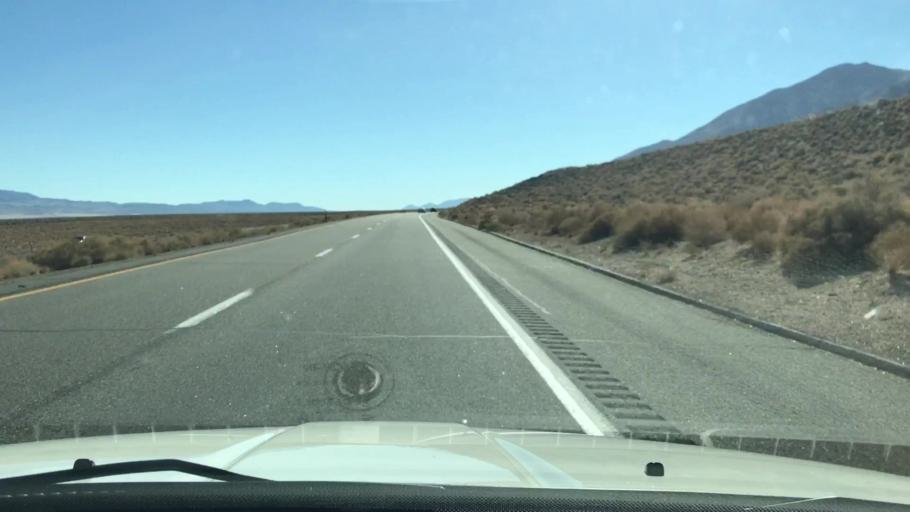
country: US
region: California
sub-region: Inyo County
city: Lone Pine
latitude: 36.4544
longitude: -118.0352
